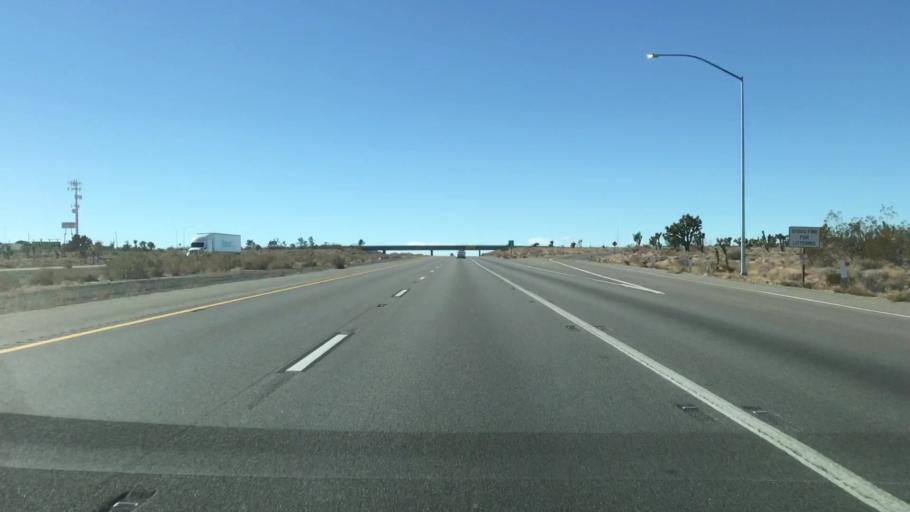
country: US
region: Nevada
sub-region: Clark County
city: Sandy Valley
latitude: 35.4045
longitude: -115.7867
